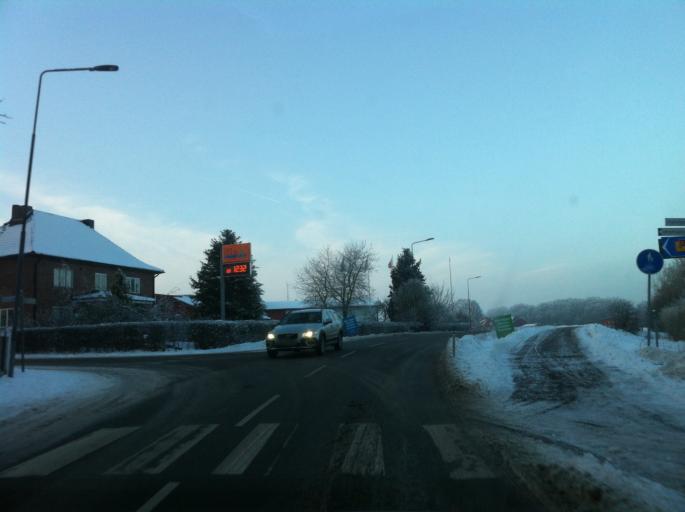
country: SE
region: Skane
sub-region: Svalovs Kommun
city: Kagerod
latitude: 55.9923
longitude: 13.0871
